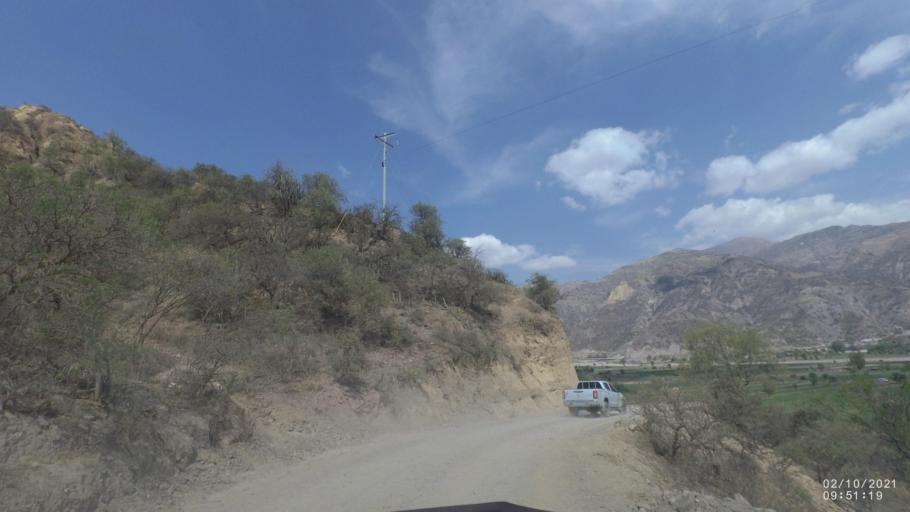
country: BO
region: Cochabamba
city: Irpa Irpa
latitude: -17.7995
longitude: -66.3399
